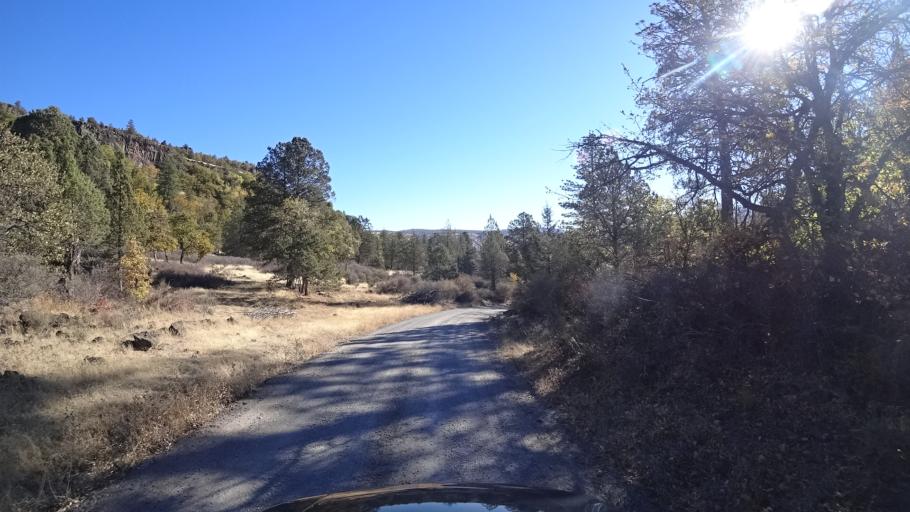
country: US
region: California
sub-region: Siskiyou County
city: Montague
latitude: 41.9859
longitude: -122.3360
